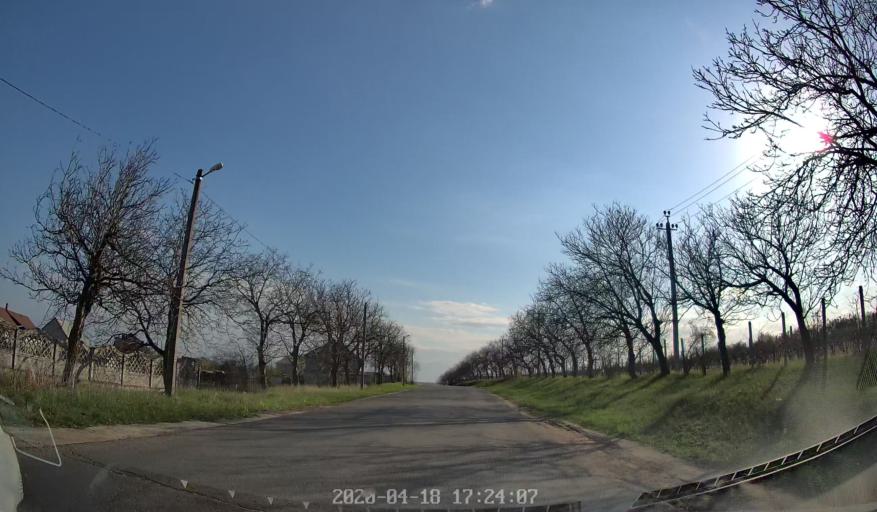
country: MD
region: Chisinau
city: Vadul lui Voda
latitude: 47.0699
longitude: 29.0170
